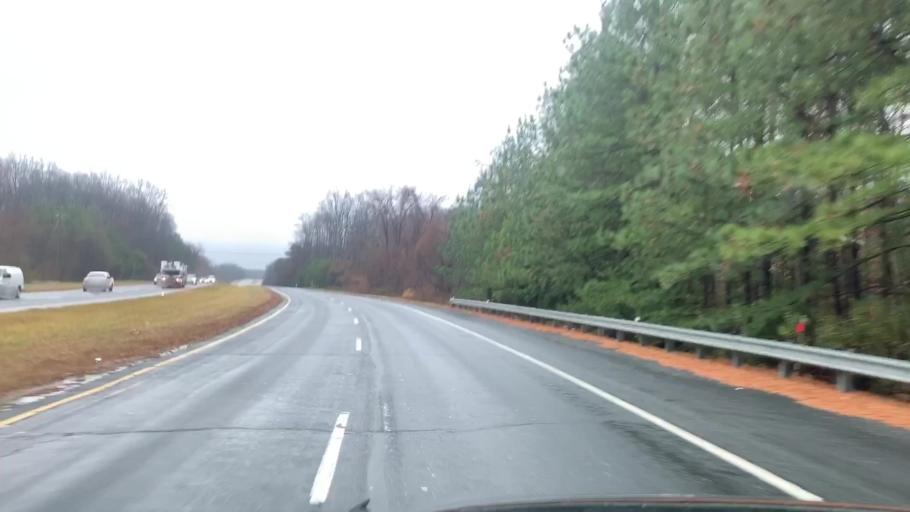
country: US
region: Virginia
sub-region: Fairfax County
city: Fairfax Station
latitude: 38.7769
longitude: -77.3260
